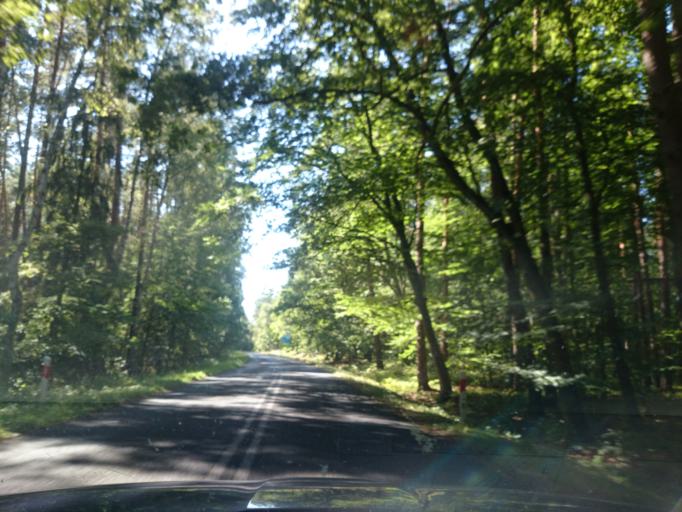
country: PL
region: West Pomeranian Voivodeship
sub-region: Powiat policki
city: Nowe Warpno
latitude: 53.6705
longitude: 14.4138
